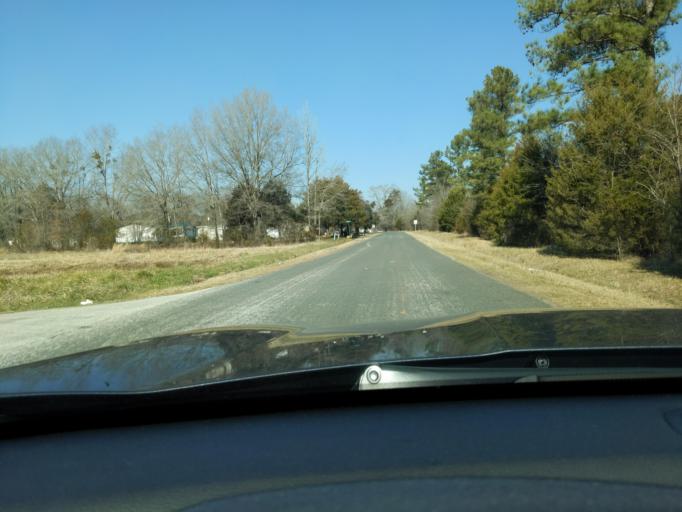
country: US
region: South Carolina
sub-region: Abbeville County
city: Calhoun Falls
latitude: 34.0830
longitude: -82.5792
